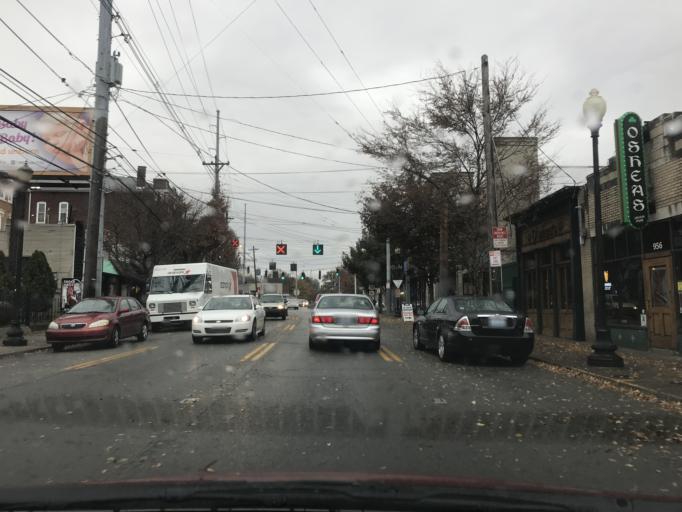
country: US
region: Kentucky
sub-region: Jefferson County
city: Audubon Park
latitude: 38.2409
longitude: -85.7248
